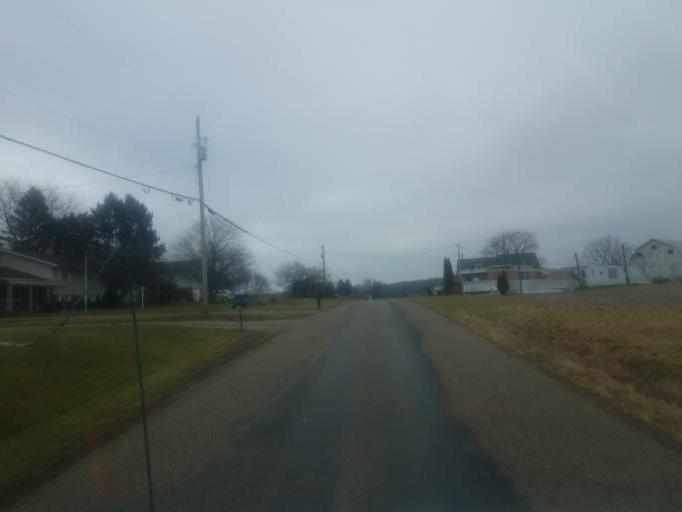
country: US
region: Ohio
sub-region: Richland County
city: Lexington
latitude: 40.6667
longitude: -82.5584
